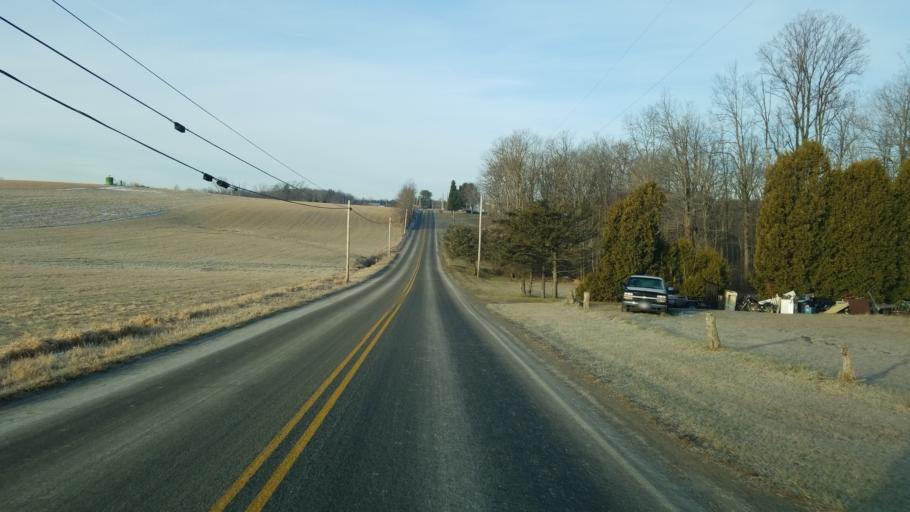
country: US
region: Pennsylvania
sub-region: Indiana County
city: Chevy Chase Heights
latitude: 40.8697
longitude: -79.1989
